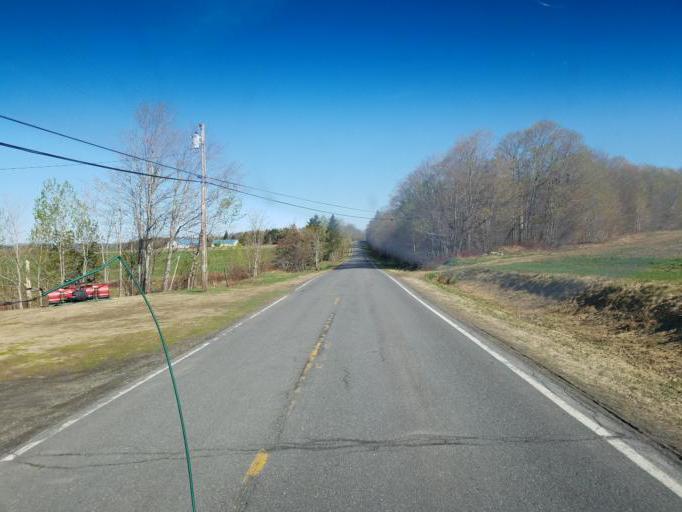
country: US
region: Maine
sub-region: Aroostook County
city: Caribou
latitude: 46.8704
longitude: -68.2117
